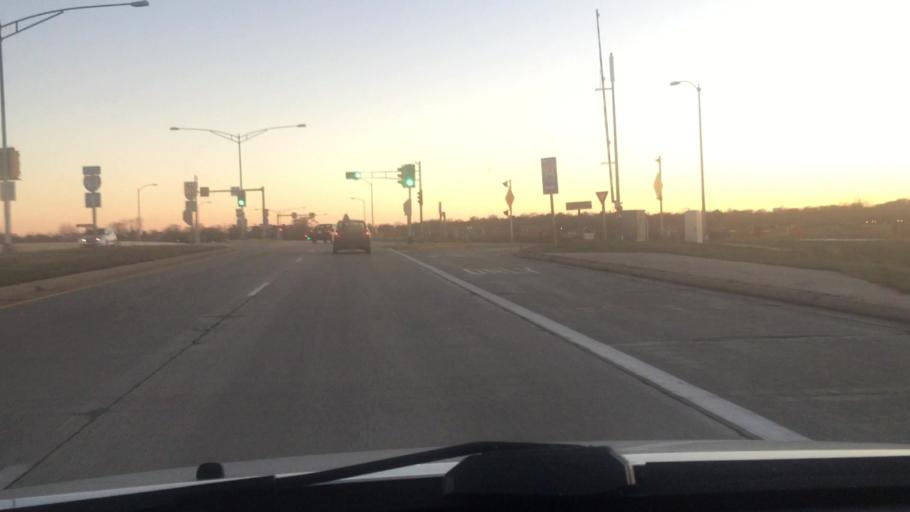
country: US
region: Wisconsin
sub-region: Waukesha County
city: Pewaukee
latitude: 43.0481
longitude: -88.2561
